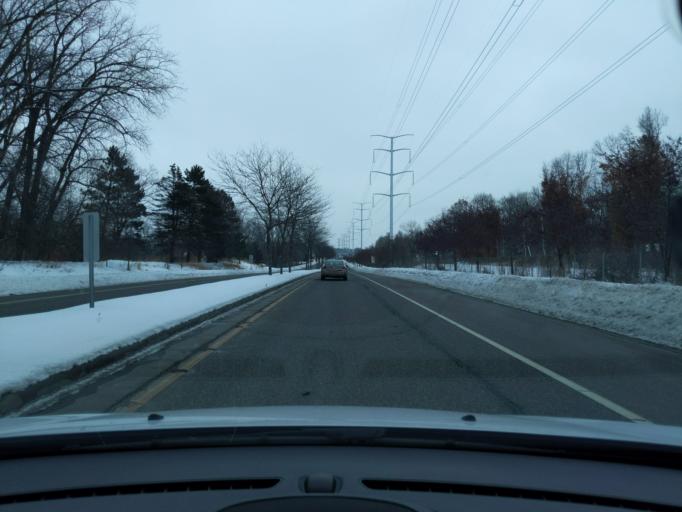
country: US
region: Minnesota
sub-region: Ramsey County
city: Roseville
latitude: 45.0206
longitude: -93.1554
